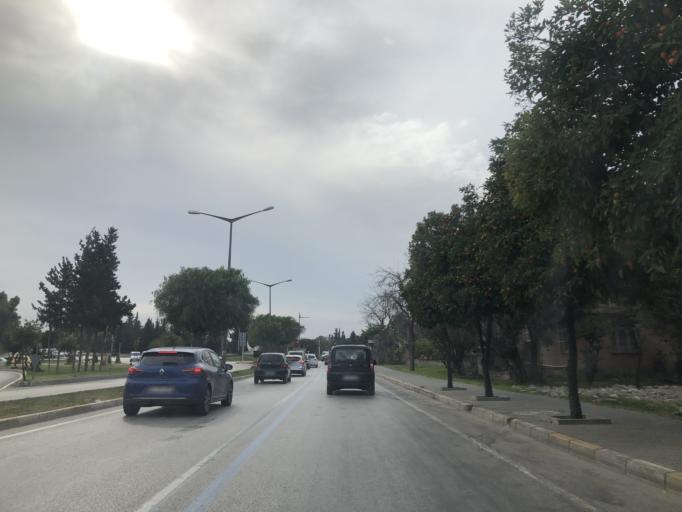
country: TR
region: Adana
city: Adana
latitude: 37.0104
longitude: 35.3370
